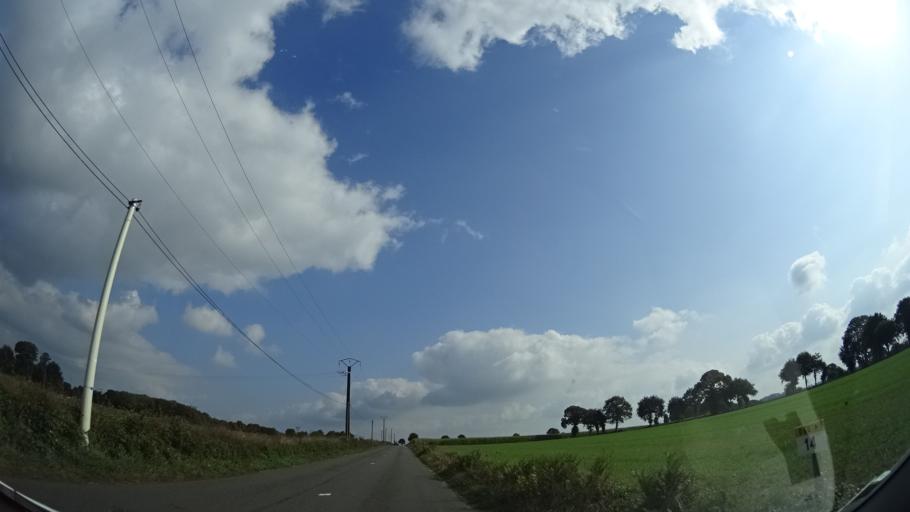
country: FR
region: Brittany
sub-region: Departement d'Ille-et-Vilaine
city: Romille
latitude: 48.2028
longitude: -1.9015
